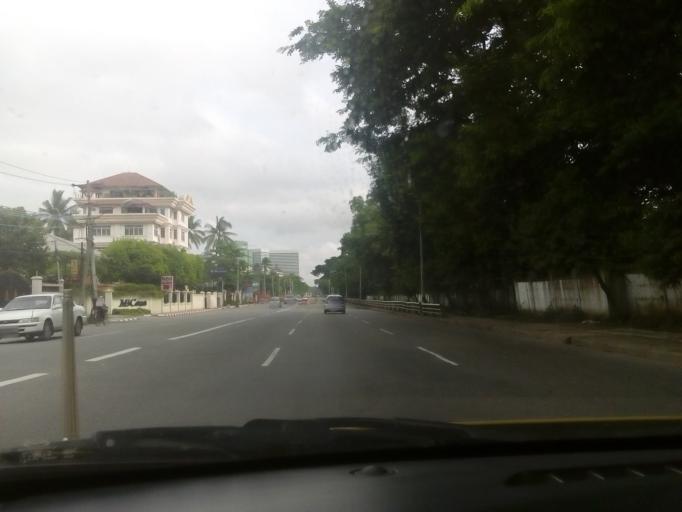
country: MM
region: Yangon
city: Yangon
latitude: 16.8411
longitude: 96.1563
